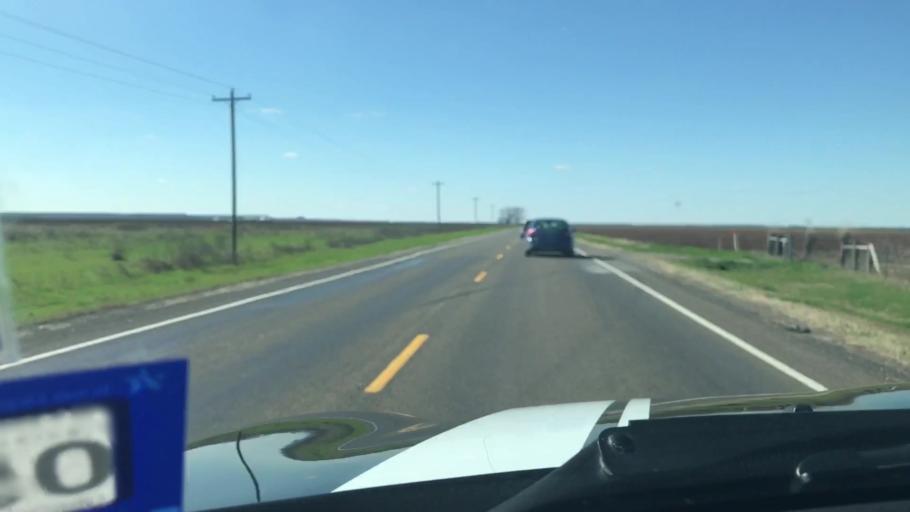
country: US
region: Texas
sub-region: Robertson County
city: Hearne
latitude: 30.8766
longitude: -96.6494
